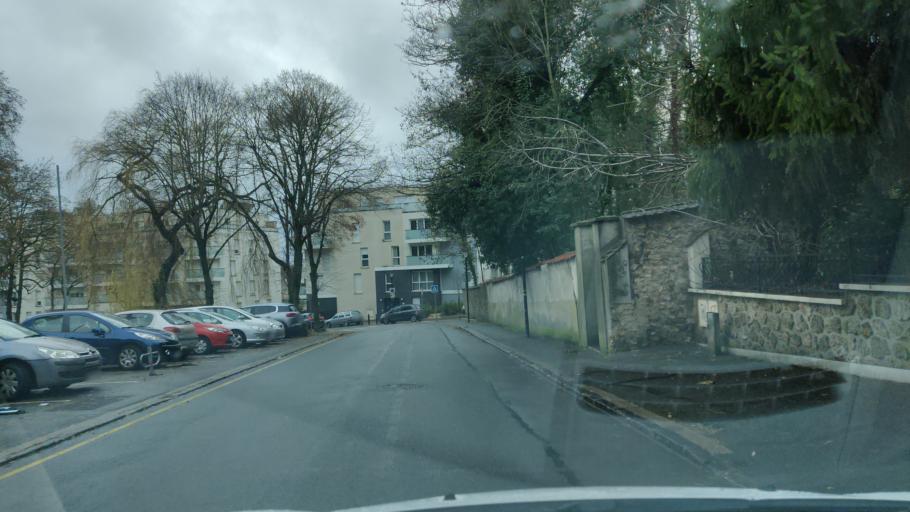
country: FR
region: Ile-de-France
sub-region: Departement de Seine-et-Marne
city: Thorigny-sur-Marne
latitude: 48.8834
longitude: 2.7087
